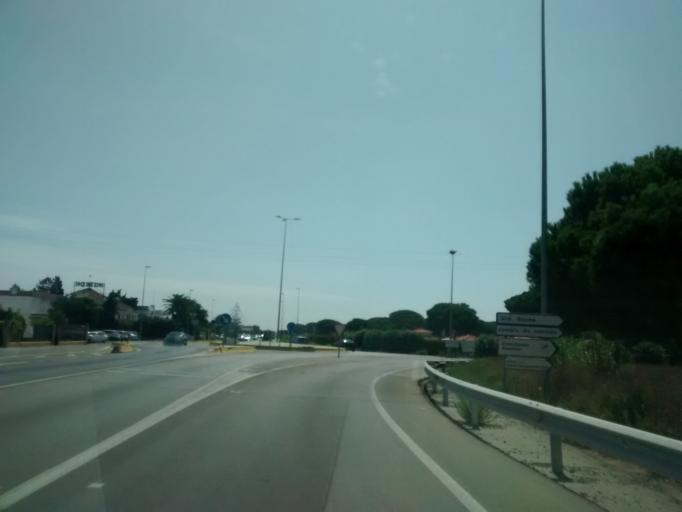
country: ES
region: Andalusia
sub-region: Provincia de Cadiz
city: Conil de la Frontera
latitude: 36.3388
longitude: -6.0936
